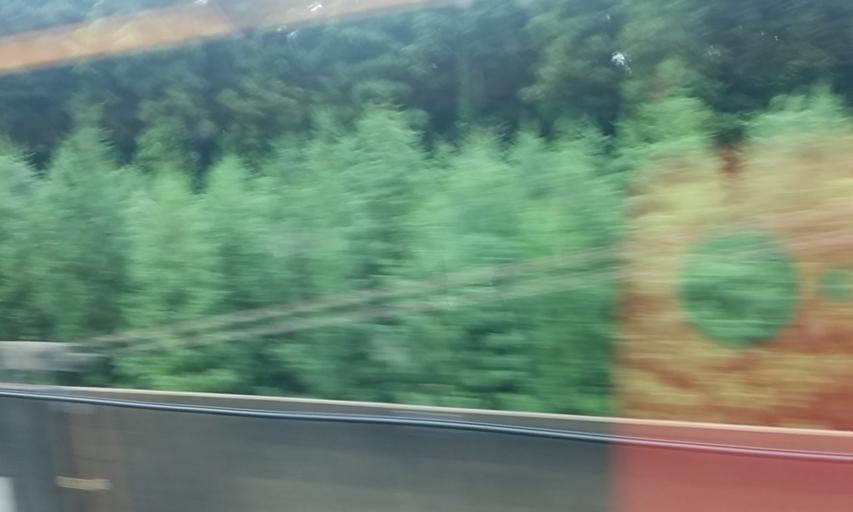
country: JP
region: Tochigi
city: Yaita
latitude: 36.8068
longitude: 139.9570
